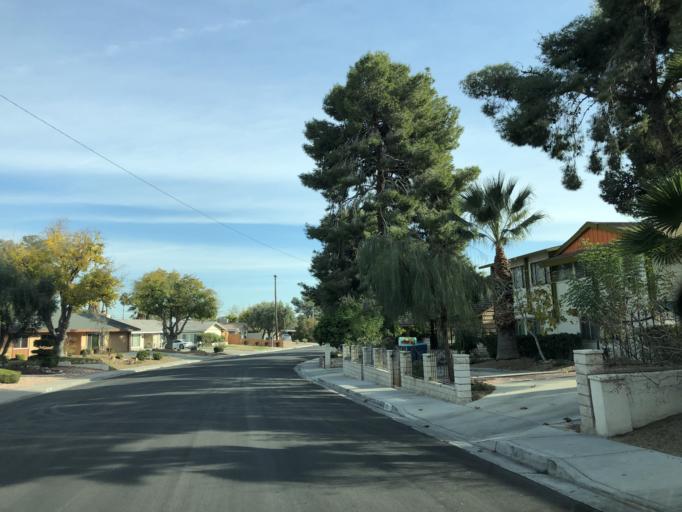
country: US
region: Nevada
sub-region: Clark County
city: Winchester
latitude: 36.1237
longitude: -115.1232
